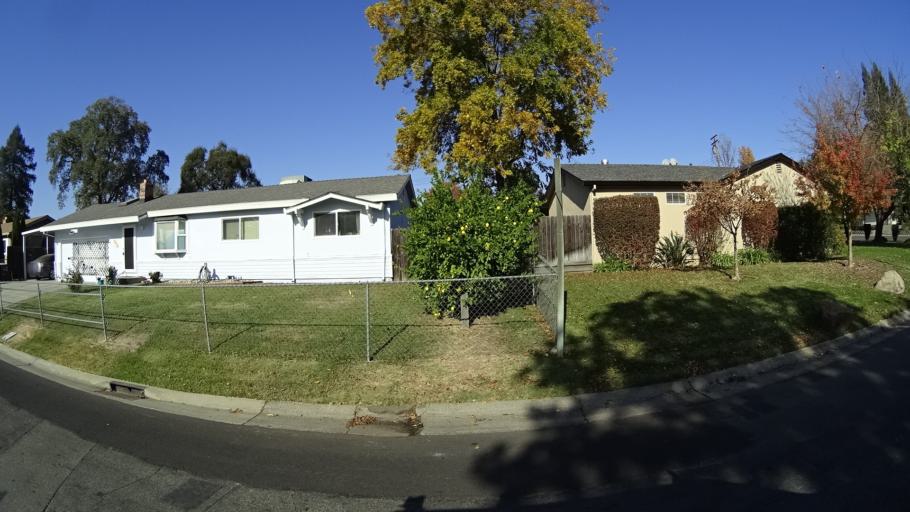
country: US
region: California
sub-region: Sacramento County
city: Citrus Heights
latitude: 38.6849
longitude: -121.2852
